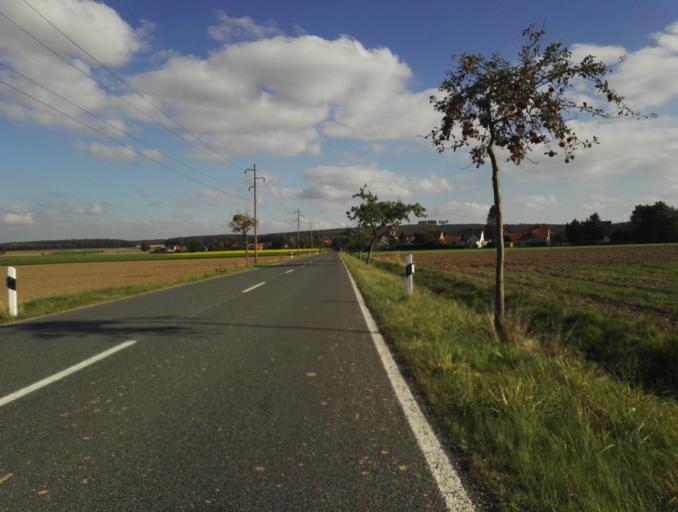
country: DE
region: Lower Saxony
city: Schellerten
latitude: 52.1480
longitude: 10.1207
